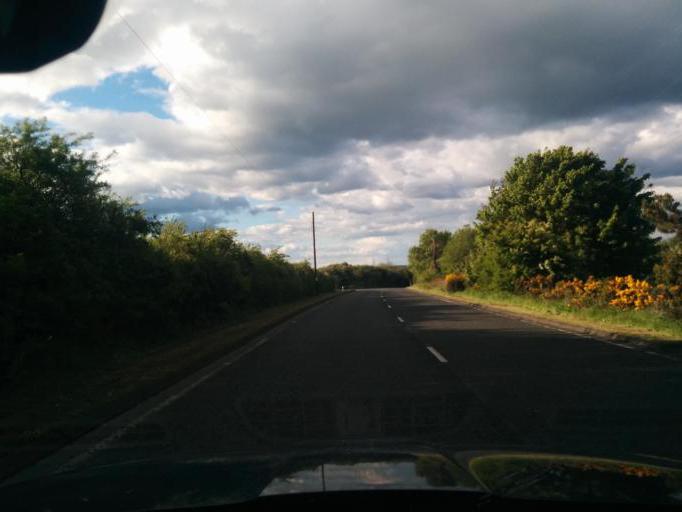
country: GB
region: England
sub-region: Northumberland
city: Cramlington
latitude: 55.0912
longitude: -1.6199
